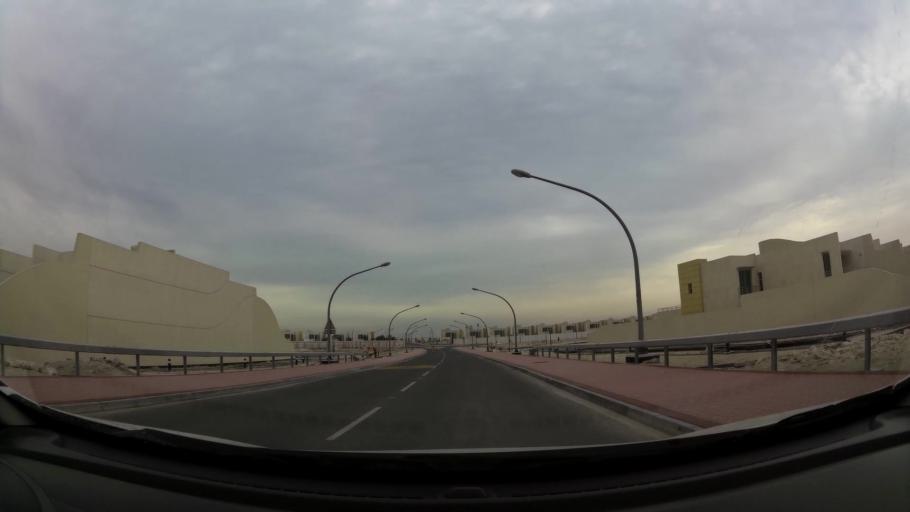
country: BH
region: Central Governorate
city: Dar Kulayb
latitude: 25.8289
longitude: 50.6089
